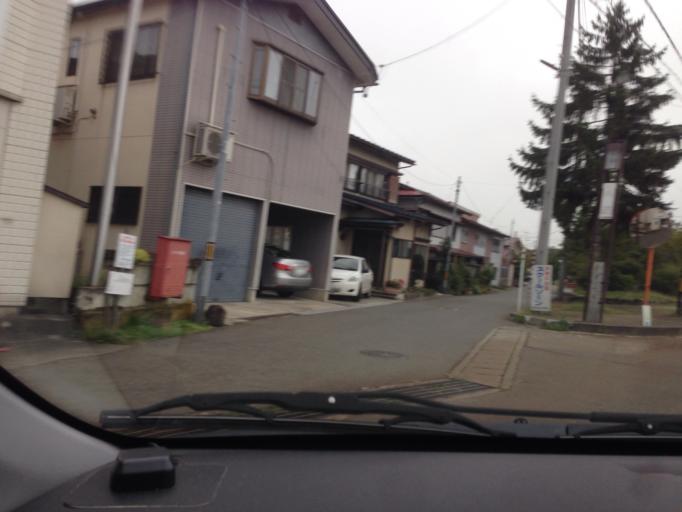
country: JP
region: Fukushima
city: Kitakata
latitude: 37.5966
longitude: 139.8906
